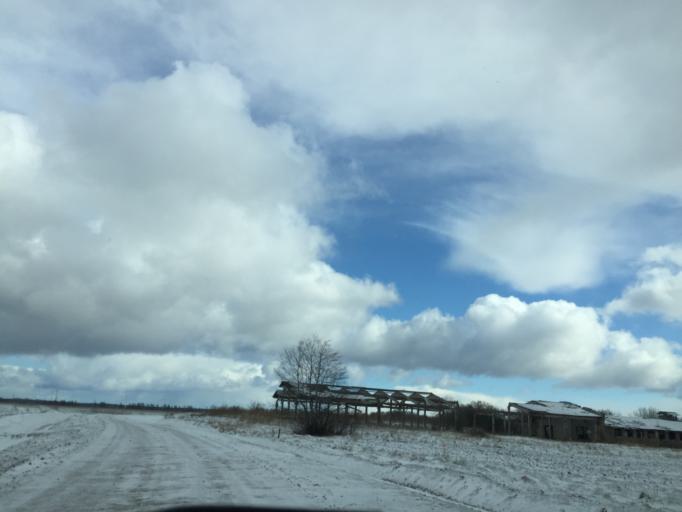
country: LV
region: Ventspils
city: Ventspils
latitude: 57.3711
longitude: 21.6286
